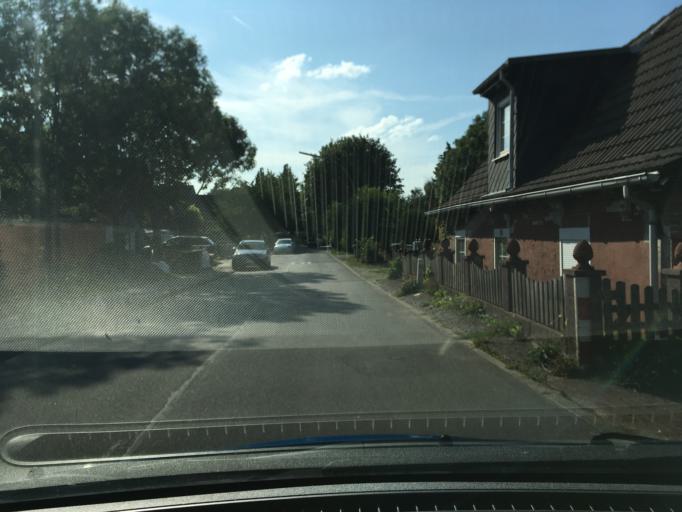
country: DE
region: Hamburg
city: Rothenburgsort
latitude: 53.5032
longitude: 10.0305
